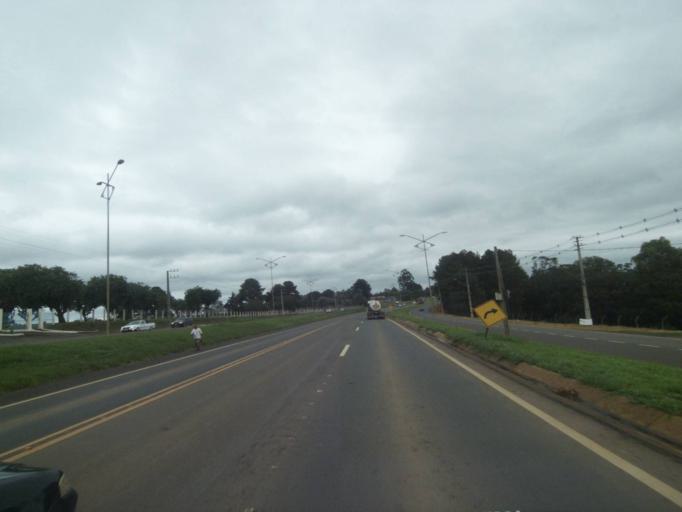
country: BR
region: Parana
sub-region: Telemaco Borba
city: Telemaco Borba
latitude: -24.3414
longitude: -50.6572
